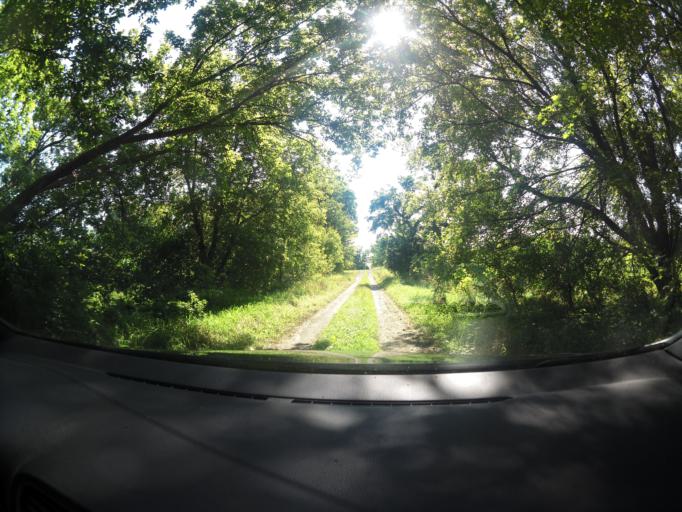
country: CA
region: Ontario
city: Arnprior
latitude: 45.3602
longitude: -76.2674
